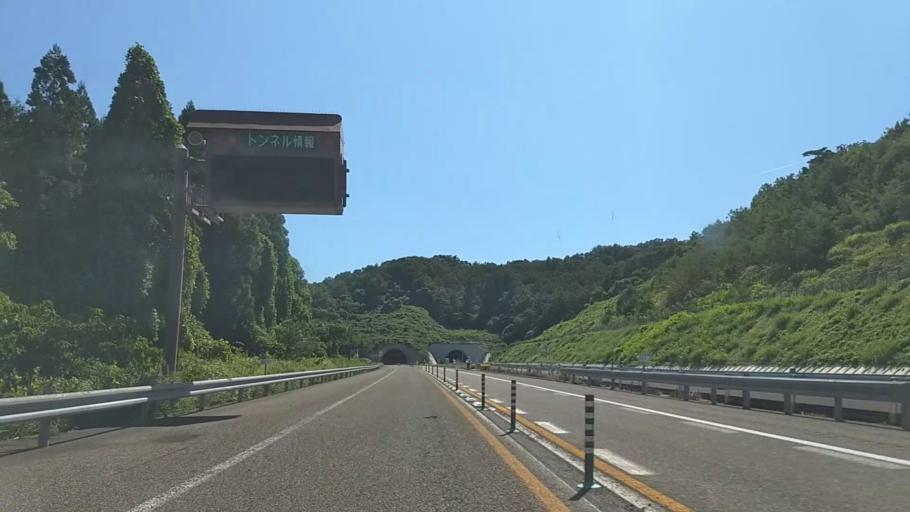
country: JP
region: Niigata
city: Joetsu
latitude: 37.1089
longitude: 138.2193
